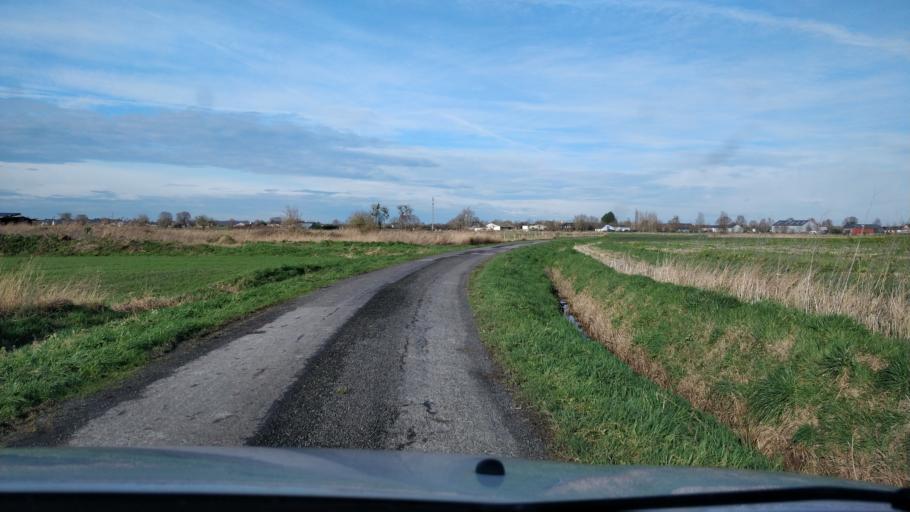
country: FR
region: Brittany
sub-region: Departement d'Ille-et-Vilaine
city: La Fresnais
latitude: 48.5780
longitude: -1.8292
